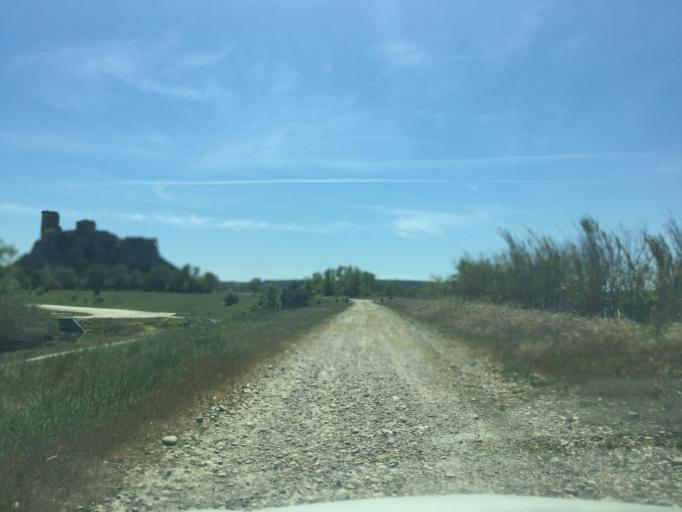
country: FR
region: Languedoc-Roussillon
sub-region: Departement du Gard
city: Roquemaure
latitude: 44.0571
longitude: 4.7904
